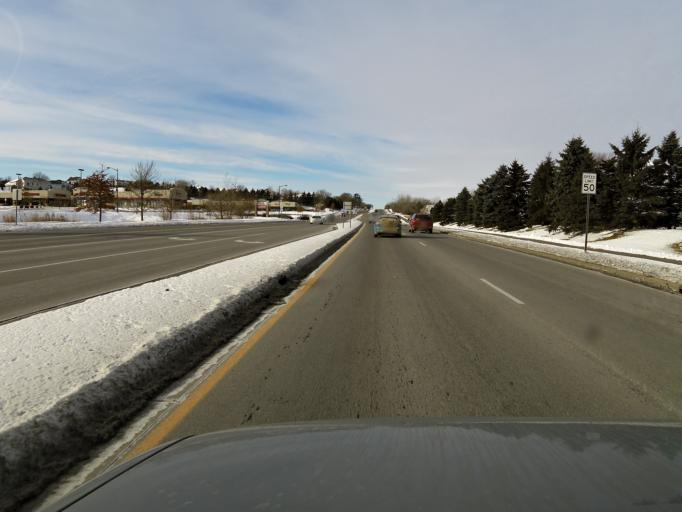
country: US
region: Minnesota
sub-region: Dakota County
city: Apple Valley
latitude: 44.7175
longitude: -93.2186
